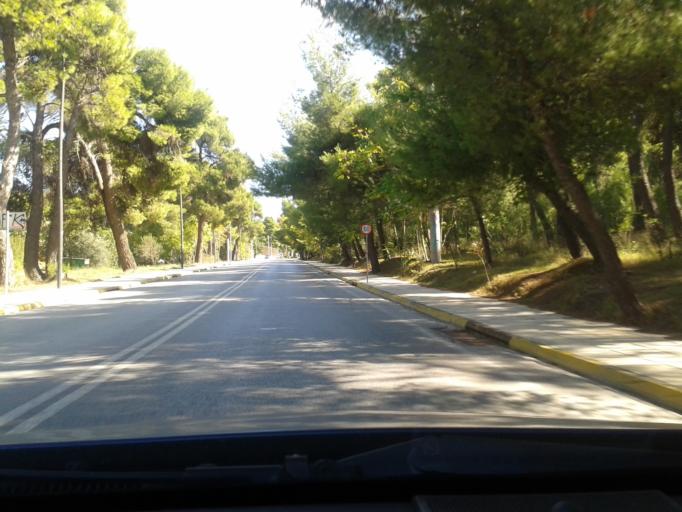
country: GR
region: Attica
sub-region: Nomarchia Anatolikis Attikis
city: Dionysos
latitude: 38.1022
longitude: 23.8802
